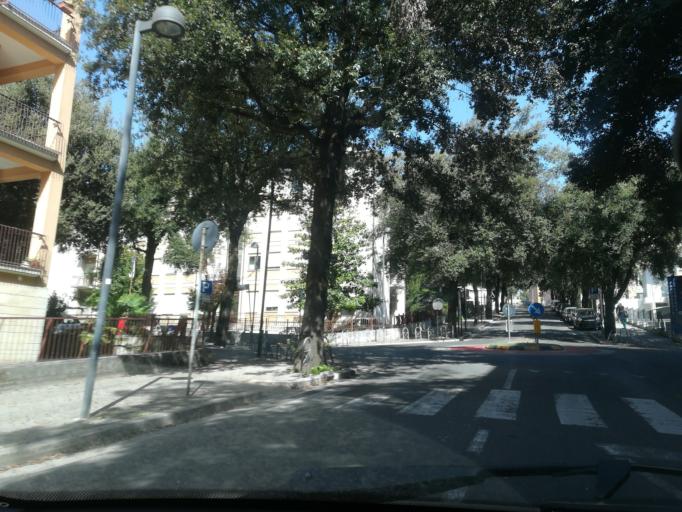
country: IT
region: The Marches
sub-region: Provincia di Macerata
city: Macerata
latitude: 43.2967
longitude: 13.4518
